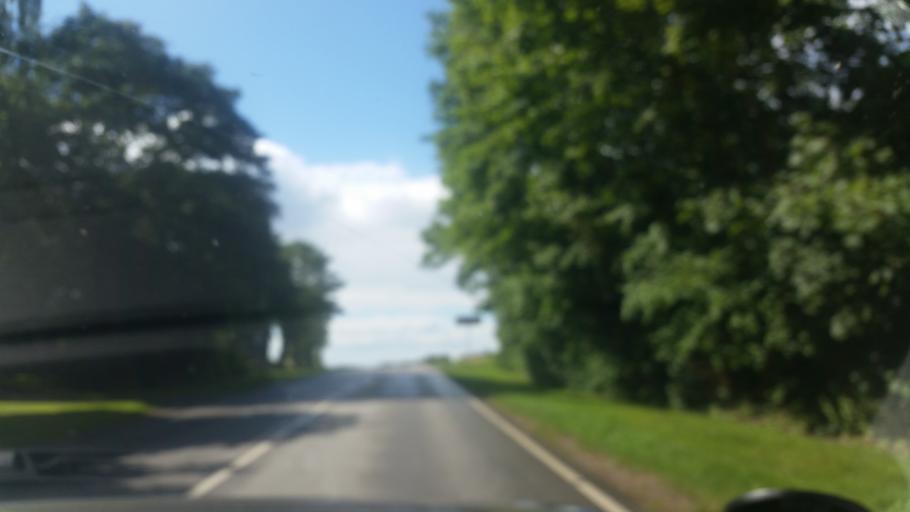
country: DK
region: Zealand
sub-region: Holbaek Kommune
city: Svinninge
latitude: 55.7378
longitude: 11.5453
